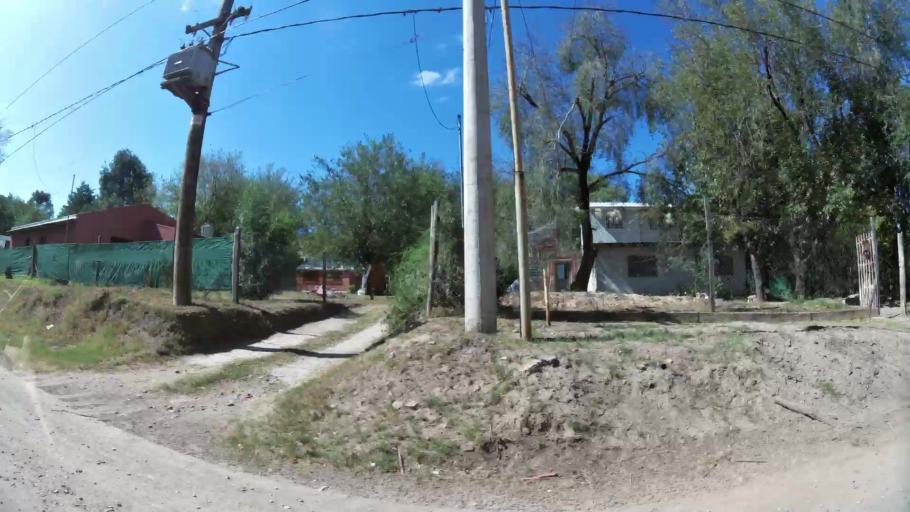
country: AR
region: Cordoba
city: Mendiolaza
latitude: -31.2687
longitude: -64.2994
